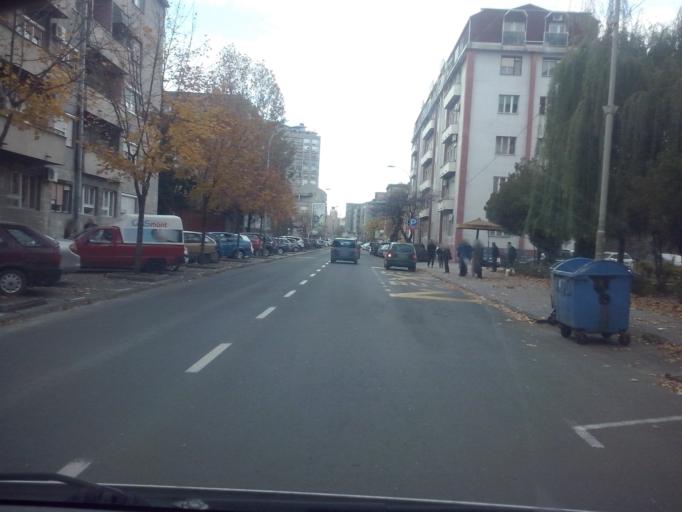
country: RS
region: Central Serbia
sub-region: Sumadijski Okrug
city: Kragujevac
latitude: 44.0148
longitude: 20.9196
